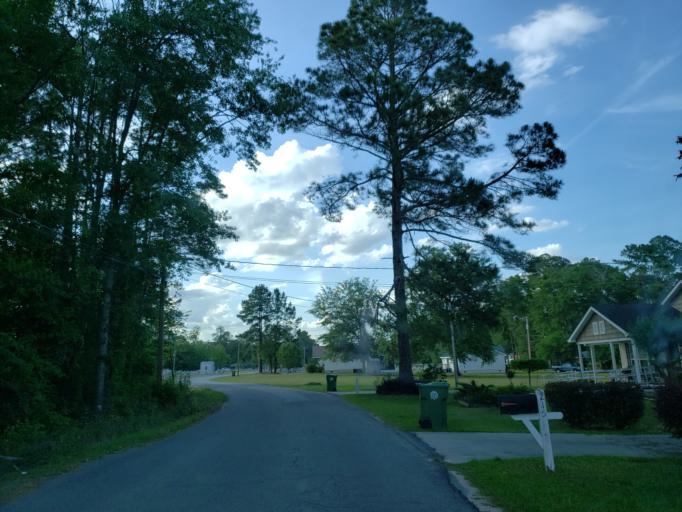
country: US
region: Georgia
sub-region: Cook County
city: Adel
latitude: 31.1362
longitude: -83.4171
